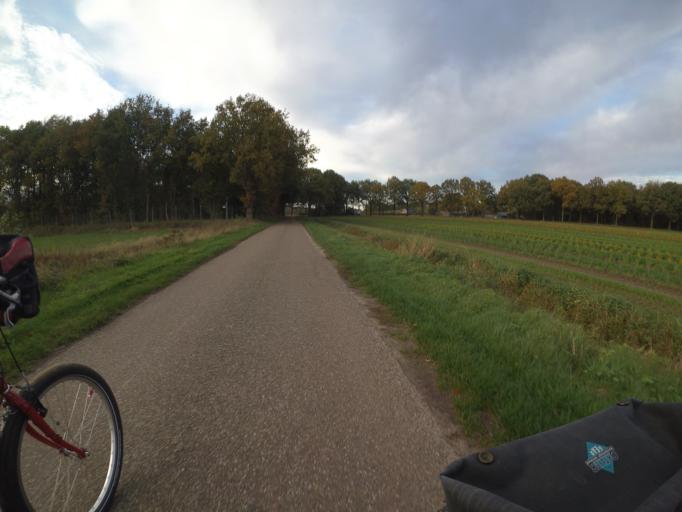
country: NL
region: North Brabant
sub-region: Gemeente Haaren
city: Haaren
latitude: 51.6140
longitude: 5.2458
